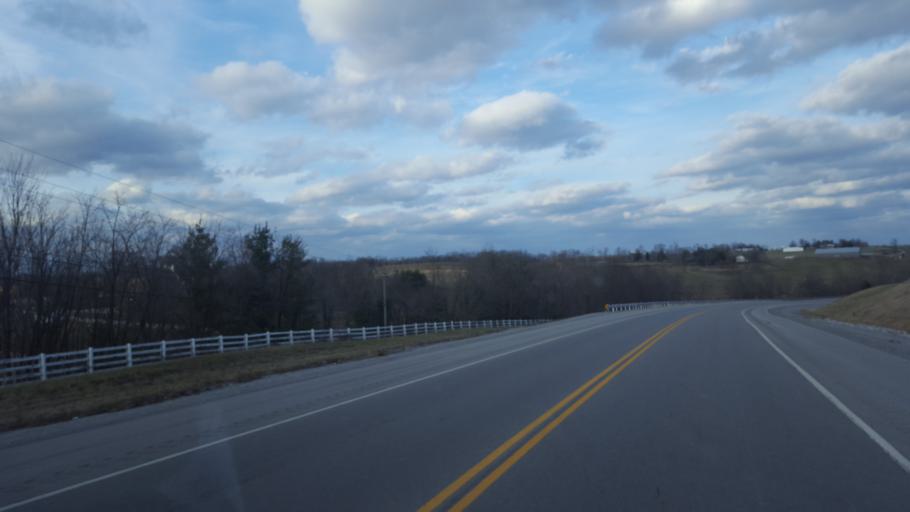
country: US
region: Kentucky
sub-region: Fleming County
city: Flemingsburg
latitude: 38.4377
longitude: -83.7104
